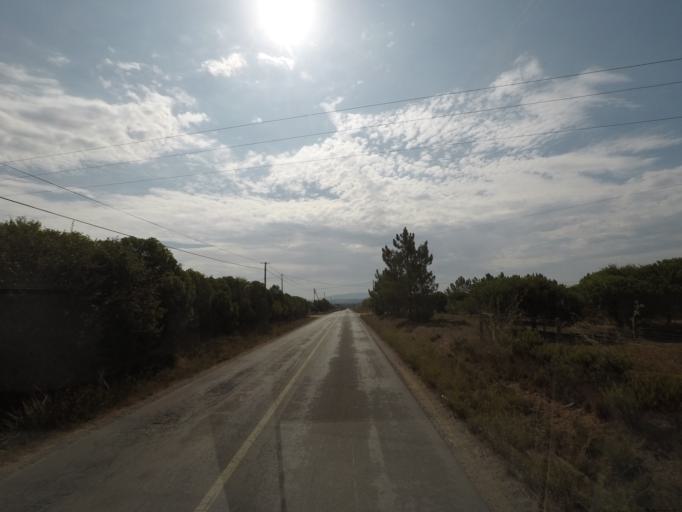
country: PT
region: Beja
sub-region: Odemira
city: Sao Teotonio
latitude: 37.4737
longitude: -8.7579
